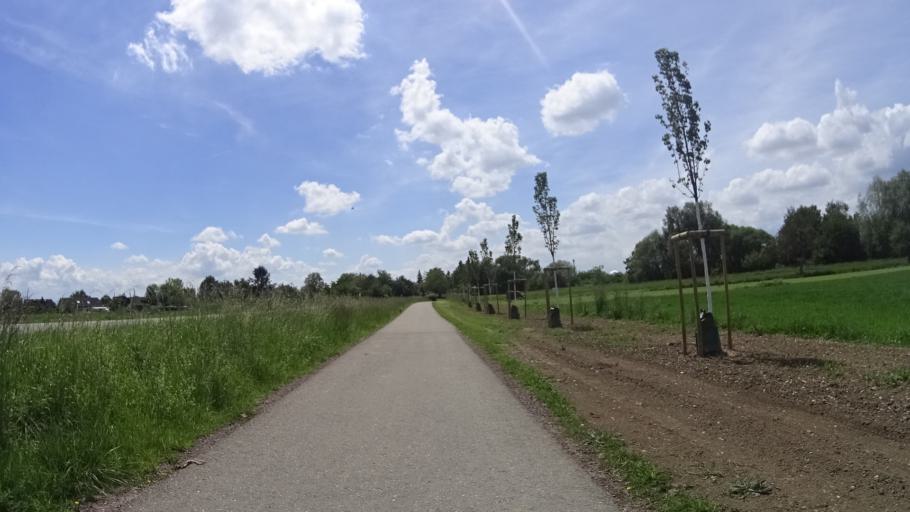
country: DE
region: Baden-Wuerttemberg
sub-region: Freiburg Region
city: Rust
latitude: 48.2756
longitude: 7.7332
